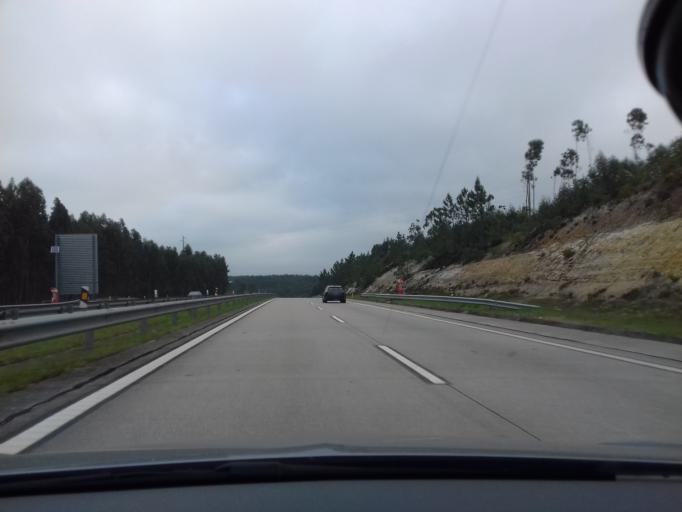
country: PT
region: Lisbon
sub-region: Torres Vedras
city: Torres Vedras
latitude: 39.1348
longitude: -9.2486
